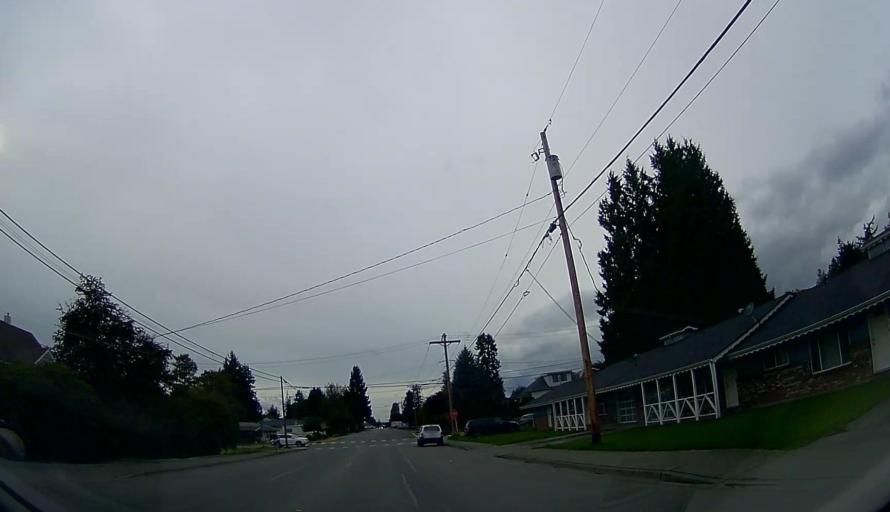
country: US
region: Washington
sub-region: Skagit County
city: Burlington
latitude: 48.4717
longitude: -122.3184
